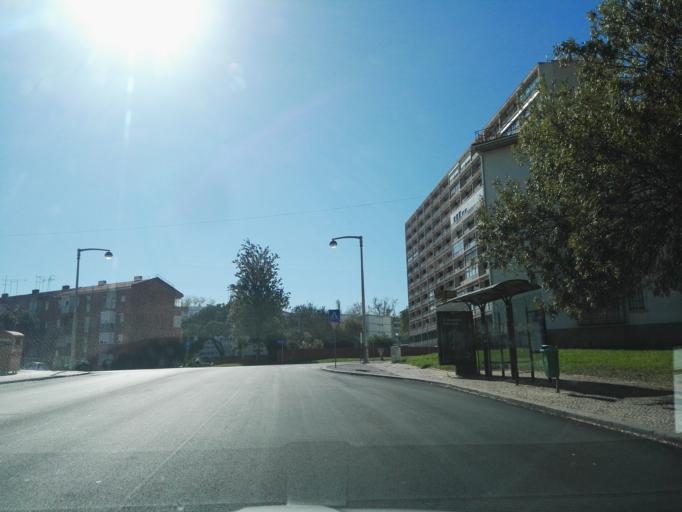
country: PT
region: Lisbon
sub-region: Loures
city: Moscavide
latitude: 38.7749
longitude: -9.1112
